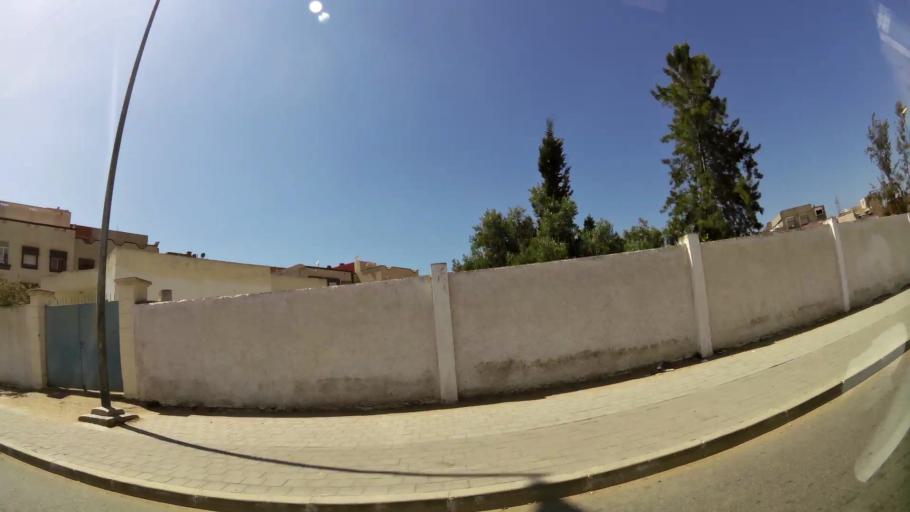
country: MA
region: Gharb-Chrarda-Beni Hssen
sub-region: Kenitra Province
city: Kenitra
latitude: 34.2360
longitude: -6.5459
